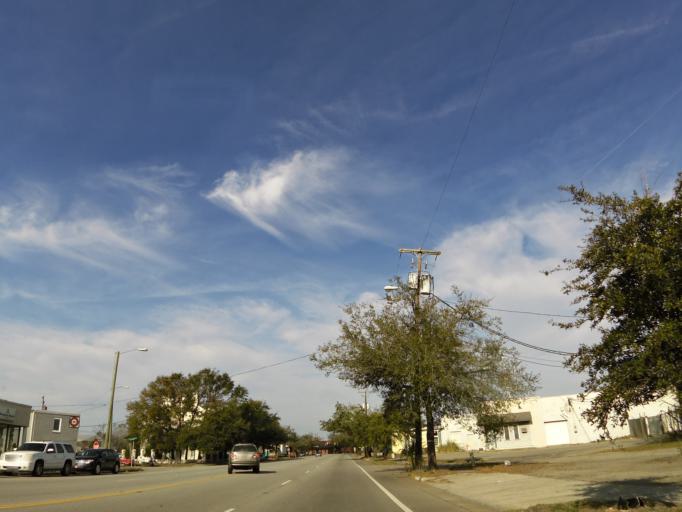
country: US
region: South Carolina
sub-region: Charleston County
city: Charleston
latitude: 32.8095
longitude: -79.9454
